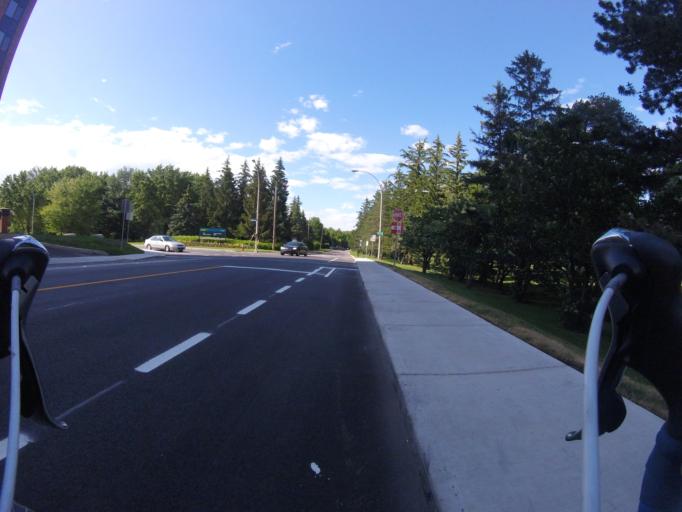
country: CA
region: Ontario
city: Ottawa
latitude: 45.4402
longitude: -75.7080
